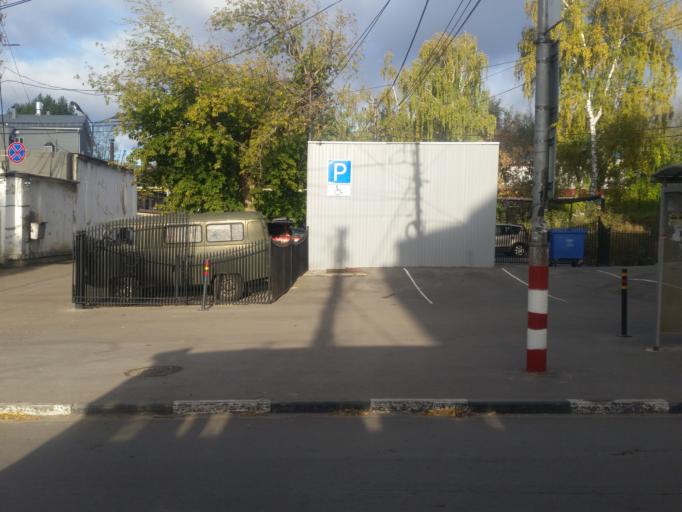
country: RU
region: Ulyanovsk
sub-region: Ulyanovskiy Rayon
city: Ulyanovsk
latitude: 54.3218
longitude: 48.3917
